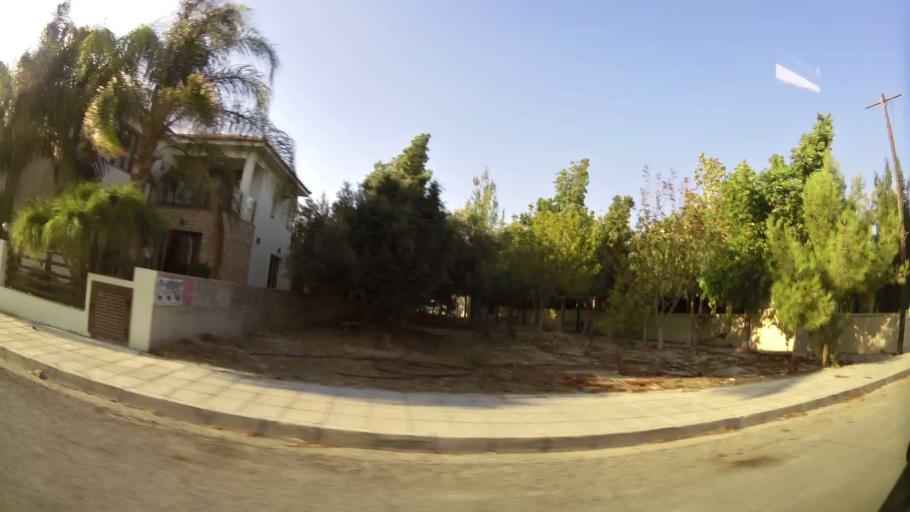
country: CY
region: Larnaka
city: Aradippou
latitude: 34.9353
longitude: 33.6038
